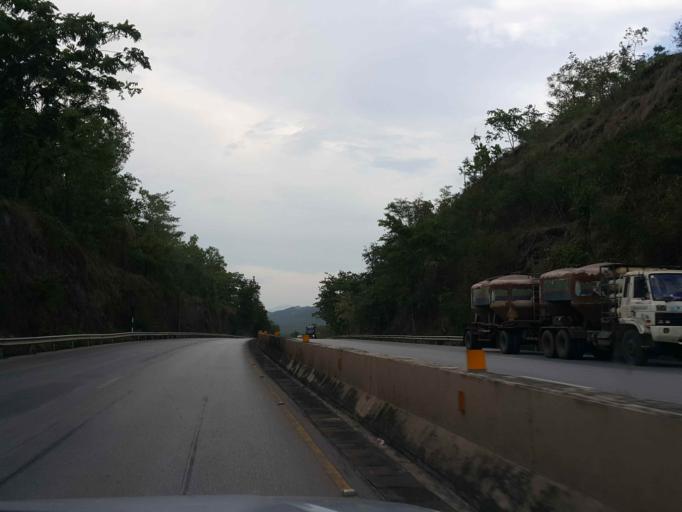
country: TH
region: Lampang
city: Soem Ngam
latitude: 18.0422
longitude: 99.3802
